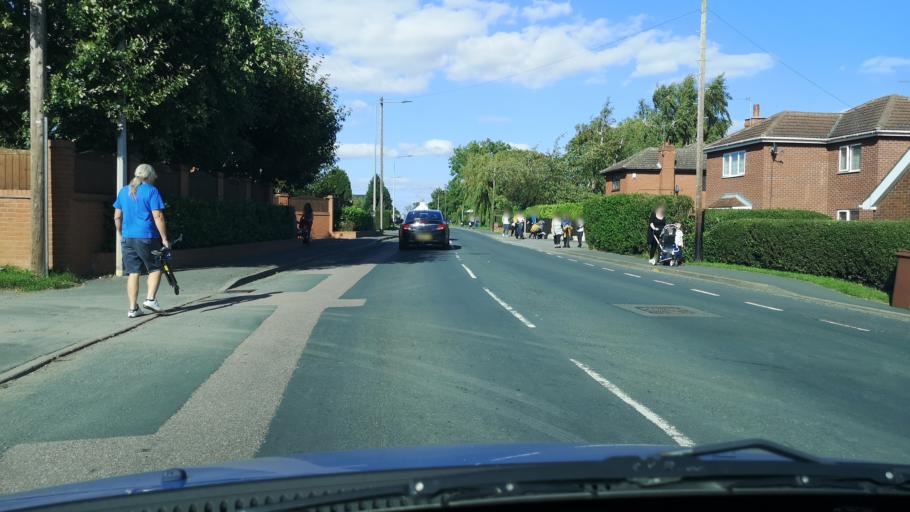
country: GB
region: England
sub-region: North Lincolnshire
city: Belton
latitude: 53.5528
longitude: -0.8168
